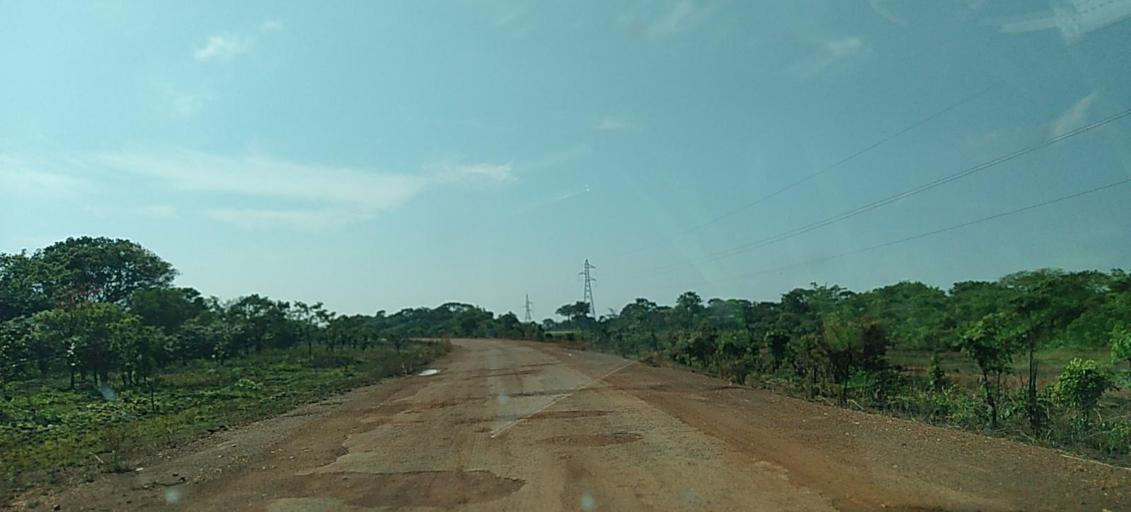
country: ZM
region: North-Western
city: Mwinilunga
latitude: -11.8194
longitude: 25.0948
